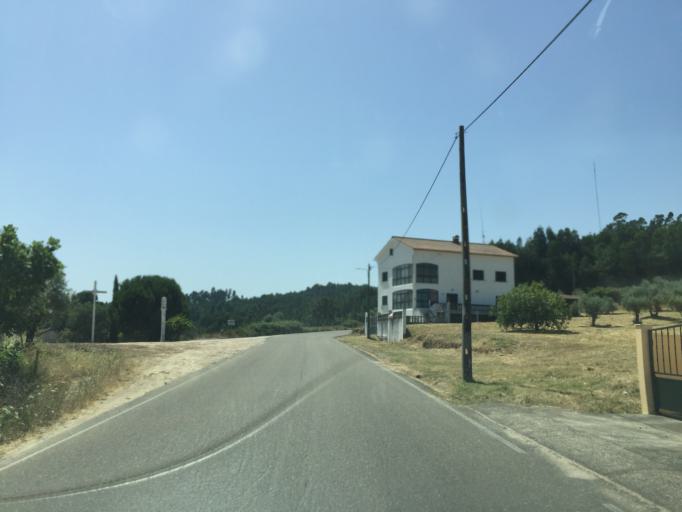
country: PT
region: Santarem
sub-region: Ferreira do Zezere
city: Ferreira do Zezere
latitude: 39.6143
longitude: -8.3116
